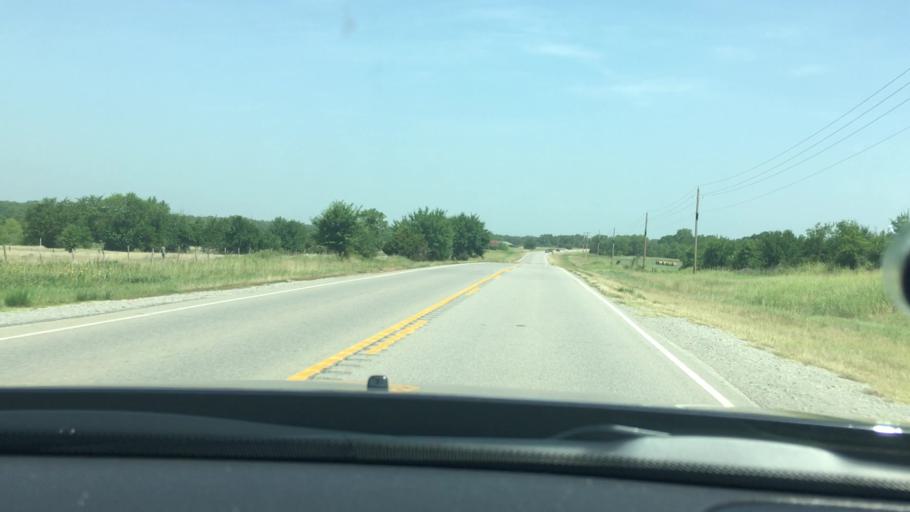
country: US
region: Oklahoma
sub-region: Coal County
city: Coalgate
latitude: 34.4574
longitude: -96.2136
